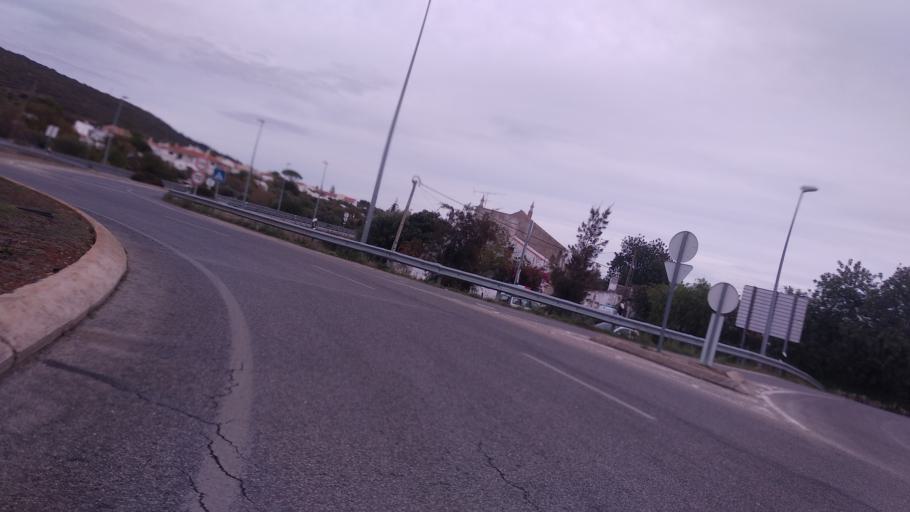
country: PT
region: Faro
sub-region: Sao Bras de Alportel
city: Sao Bras de Alportel
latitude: 37.1506
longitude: -7.9268
